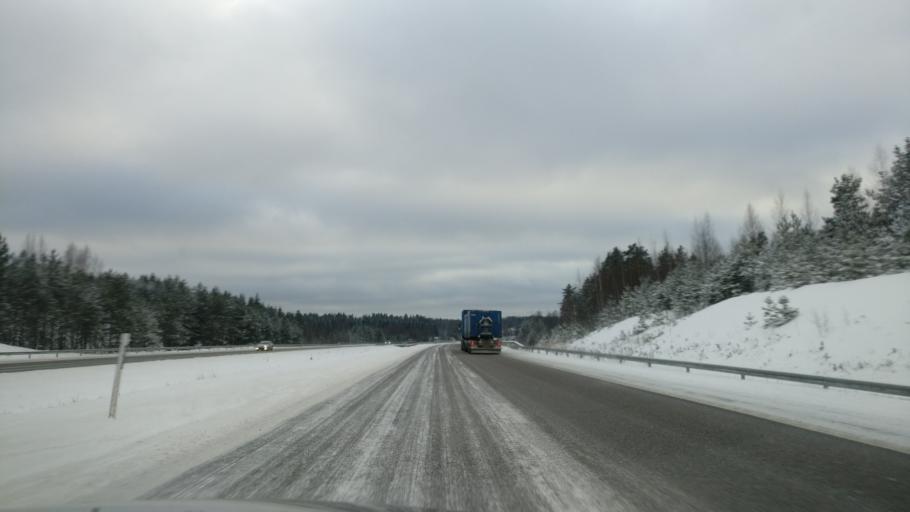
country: FI
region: Paijanne Tavastia
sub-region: Lahti
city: Nastola
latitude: 61.1036
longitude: 25.9123
